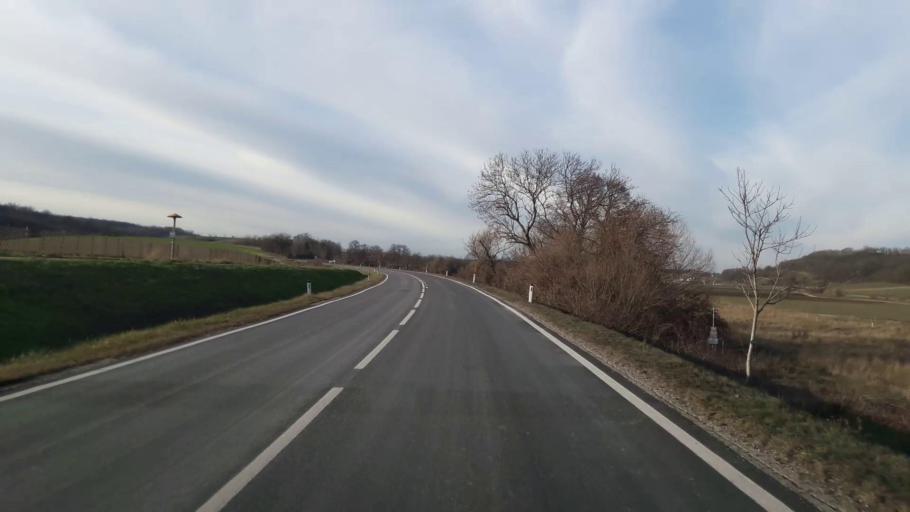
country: AT
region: Lower Austria
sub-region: Politischer Bezirk Ganserndorf
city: Gross-Schweinbarth
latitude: 48.4258
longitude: 16.6222
